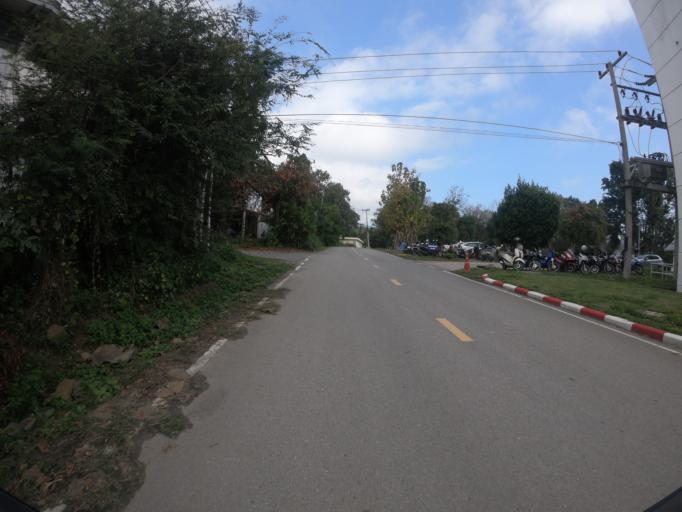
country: TH
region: Chiang Mai
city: Chiang Mai
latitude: 18.8047
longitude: 98.9477
